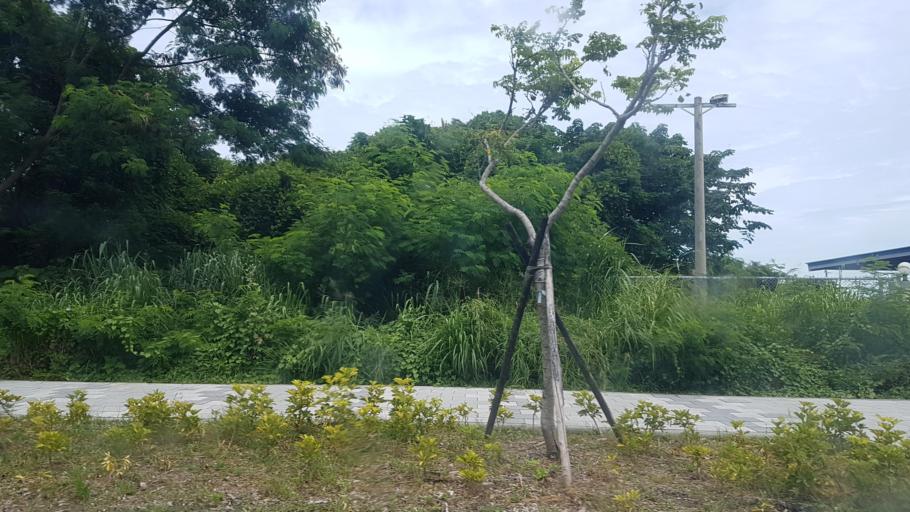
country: TW
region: Taiwan
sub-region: Hualien
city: Hualian
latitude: 24.0006
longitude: 121.6339
